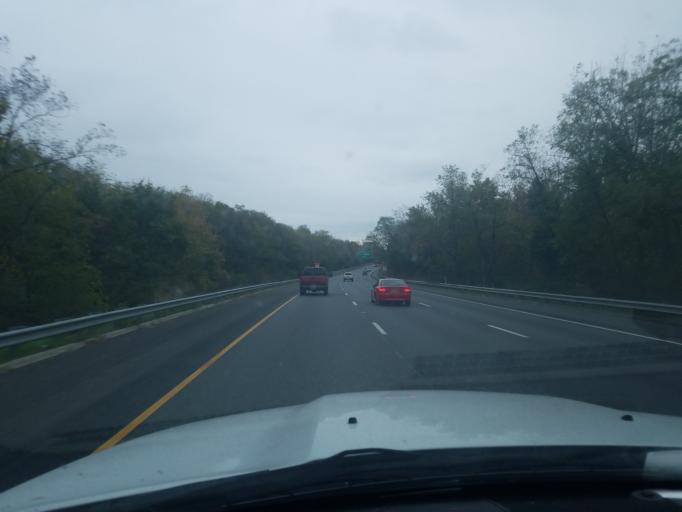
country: US
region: Indiana
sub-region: Floyd County
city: New Albany
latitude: 38.2991
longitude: -85.8460
